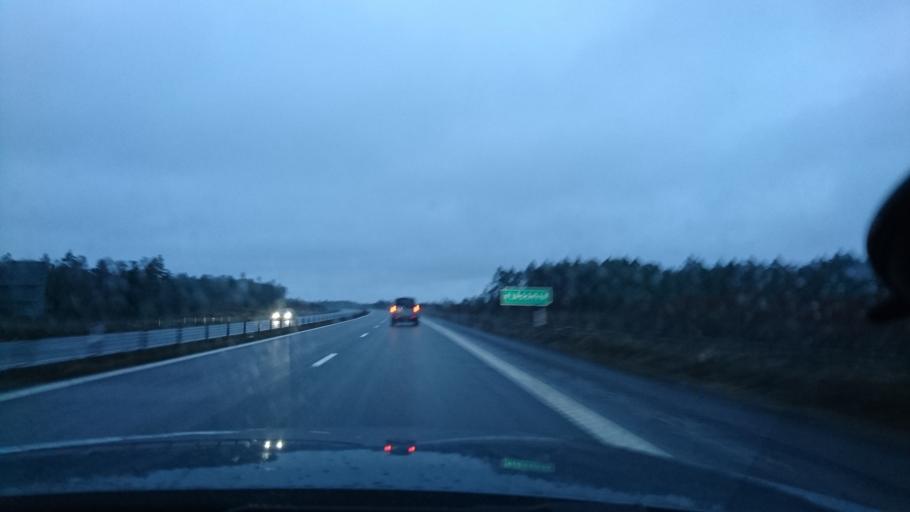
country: SE
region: Kronoberg
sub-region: Markaryds Kommun
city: Markaryd
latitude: 56.3689
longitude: 13.4966
